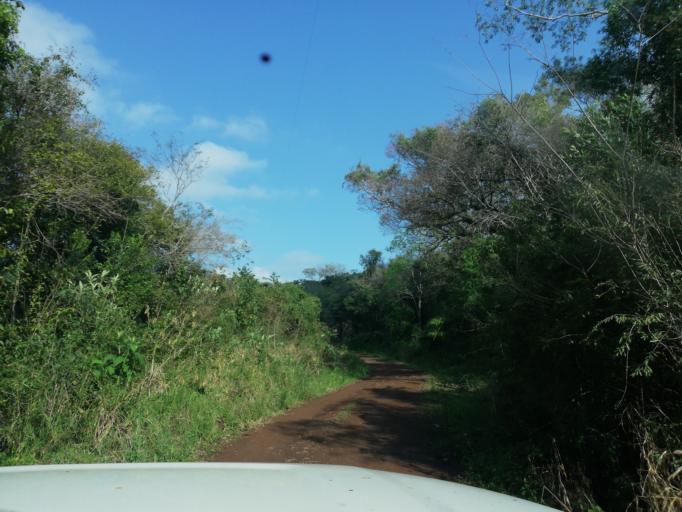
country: AR
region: Misiones
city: Cerro Azul
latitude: -27.6019
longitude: -55.5322
